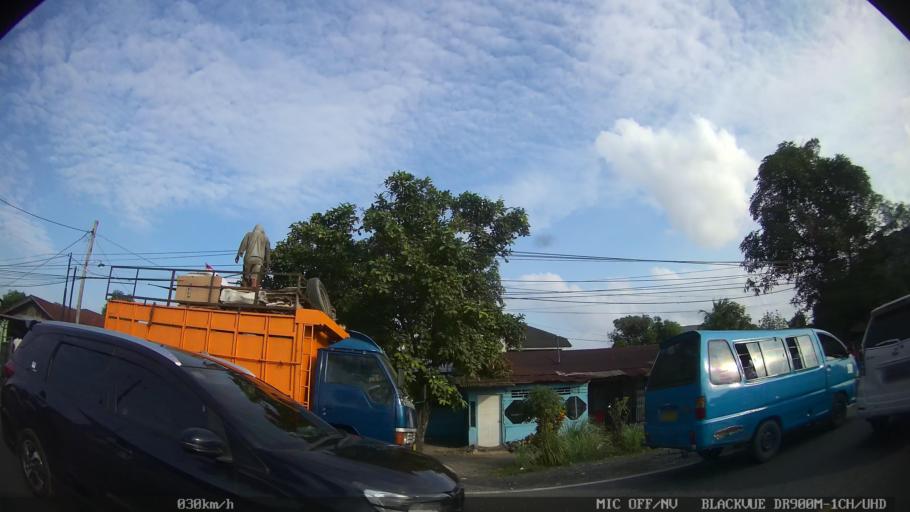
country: ID
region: North Sumatra
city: Medan
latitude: 3.6170
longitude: 98.6537
